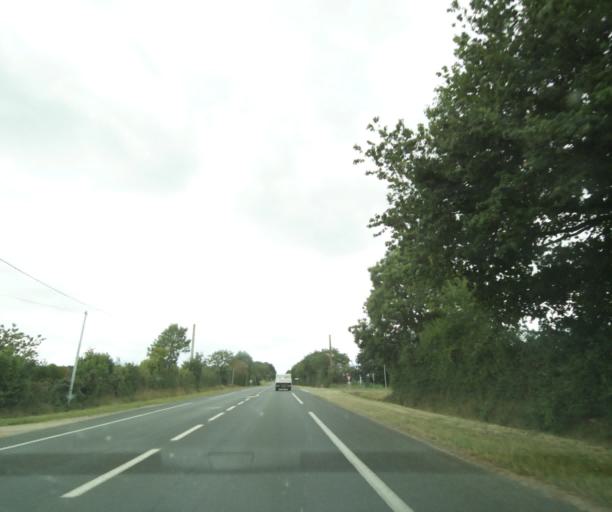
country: FR
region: Pays de la Loire
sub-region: Departement de Maine-et-Loire
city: Durtal
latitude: 47.6424
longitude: -0.2779
